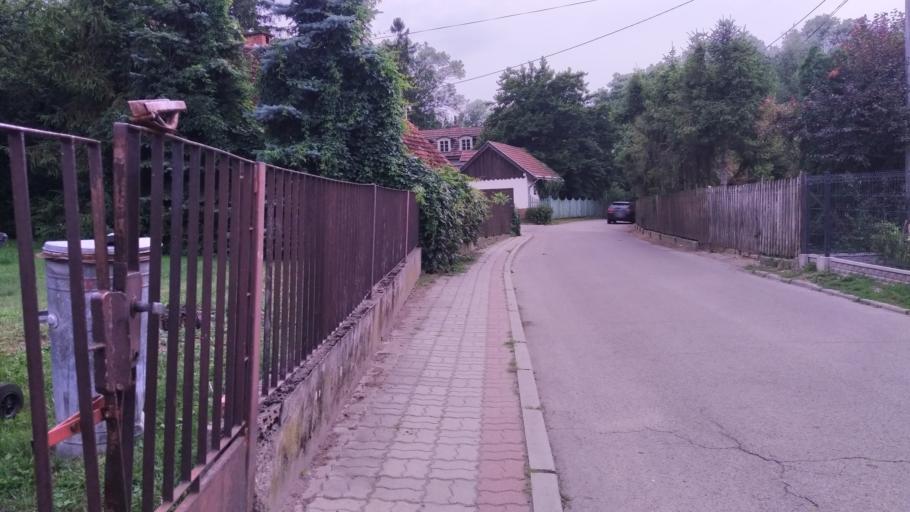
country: PL
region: Subcarpathian Voivodeship
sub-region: Powiat lancucki
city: Lancut
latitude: 50.0707
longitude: 22.2266
